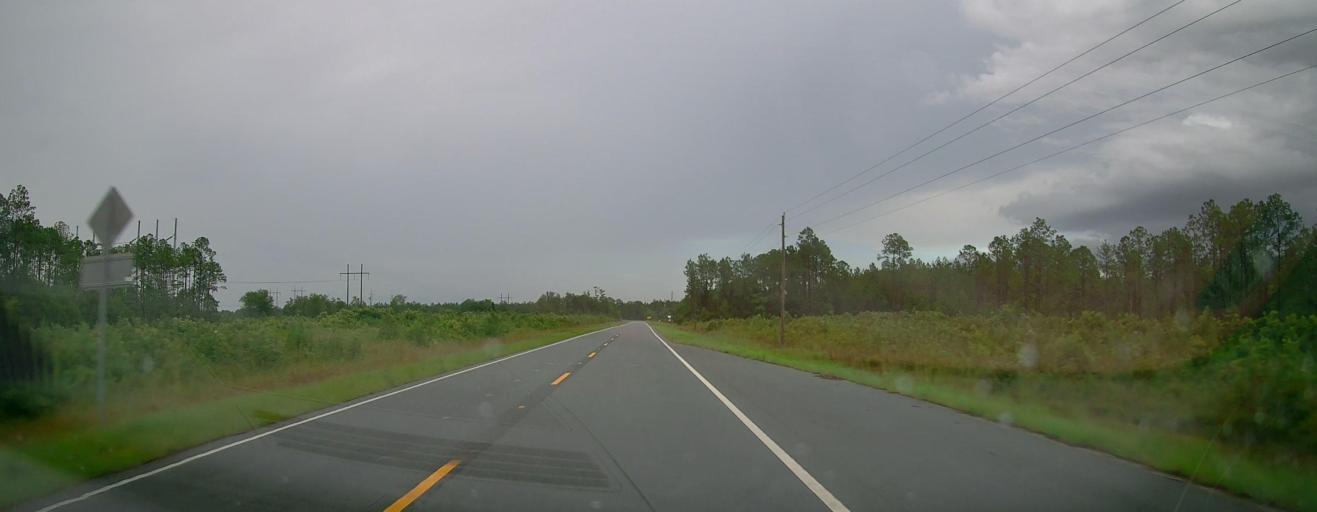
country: US
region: Georgia
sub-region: Brantley County
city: Nahunta
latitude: 31.3321
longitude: -81.9339
